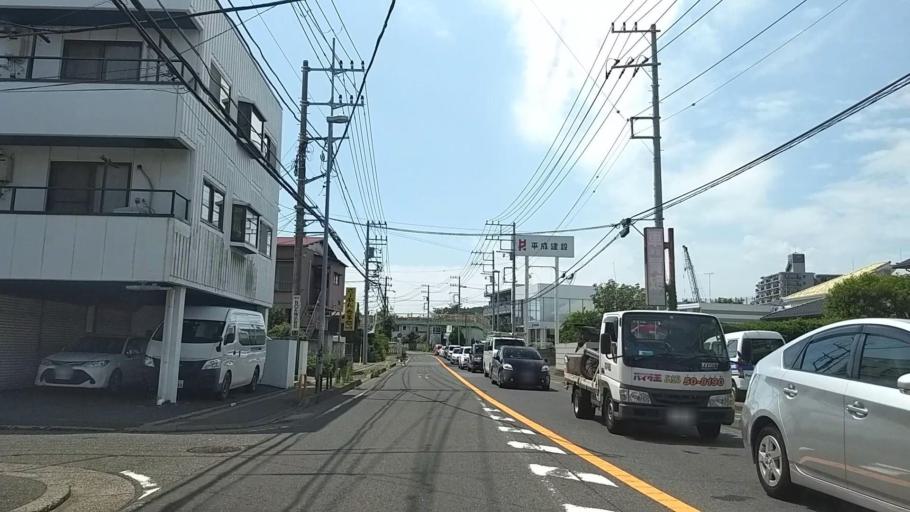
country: JP
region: Kanagawa
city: Fujisawa
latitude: 35.3474
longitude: 139.4602
